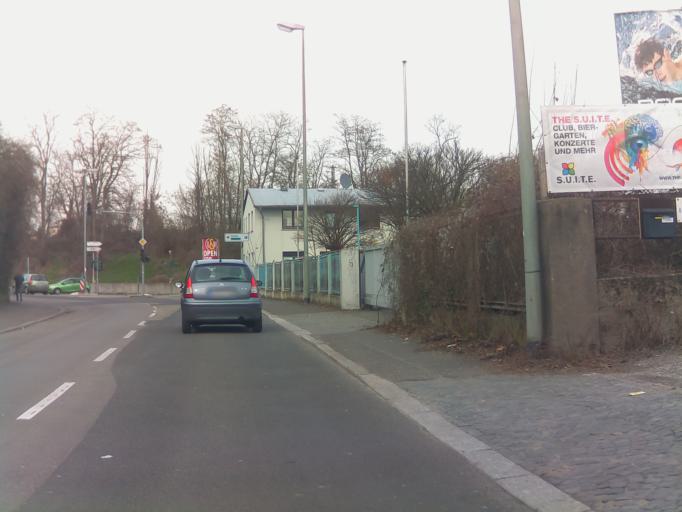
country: DE
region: Rheinland-Pfalz
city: Neustadt
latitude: 49.3489
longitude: 8.1519
